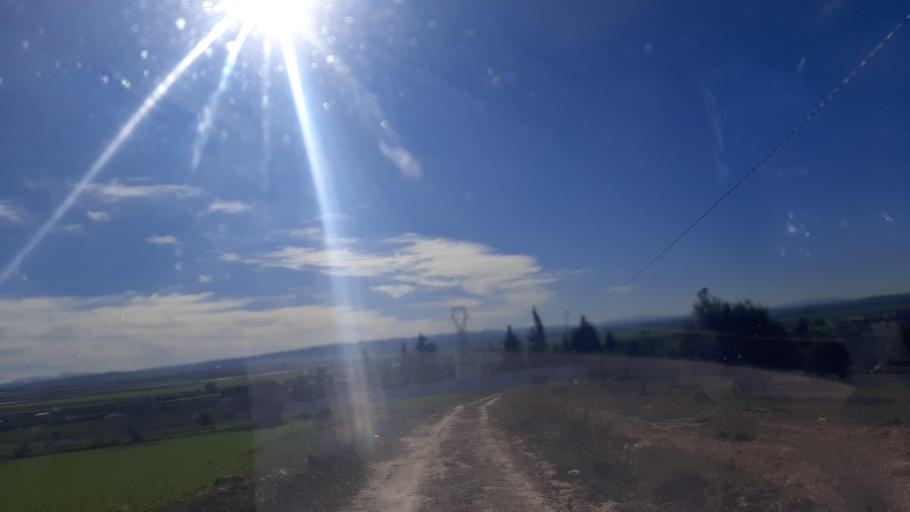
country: TN
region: Tunis
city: Oued Lill
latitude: 36.7643
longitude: 9.9854
